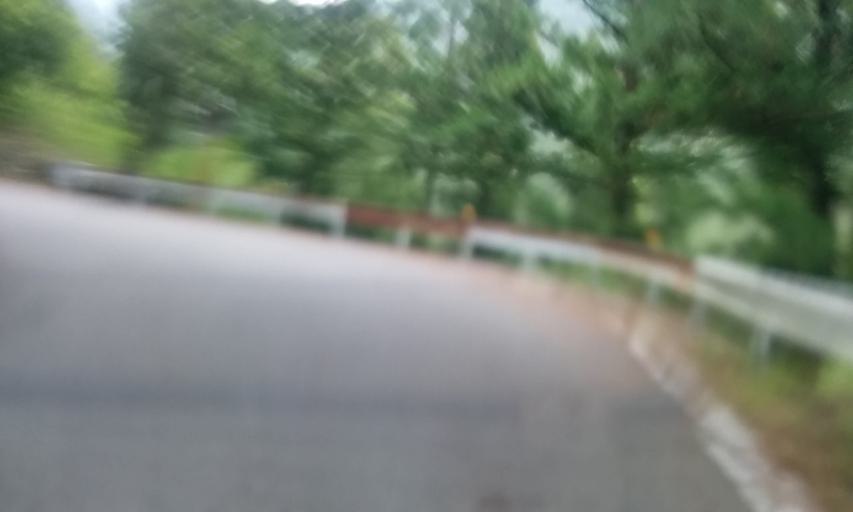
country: JP
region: Ehime
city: Saijo
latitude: 33.8029
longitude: 133.2810
